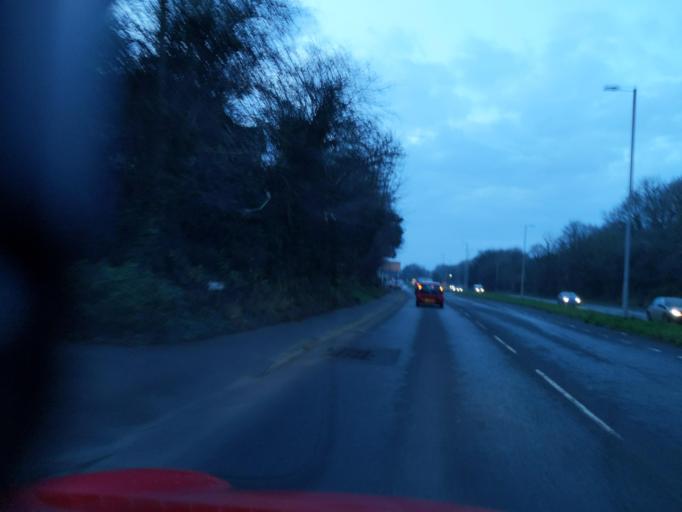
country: GB
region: England
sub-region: Plymouth
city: Plymstock
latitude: 50.3658
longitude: -4.0885
